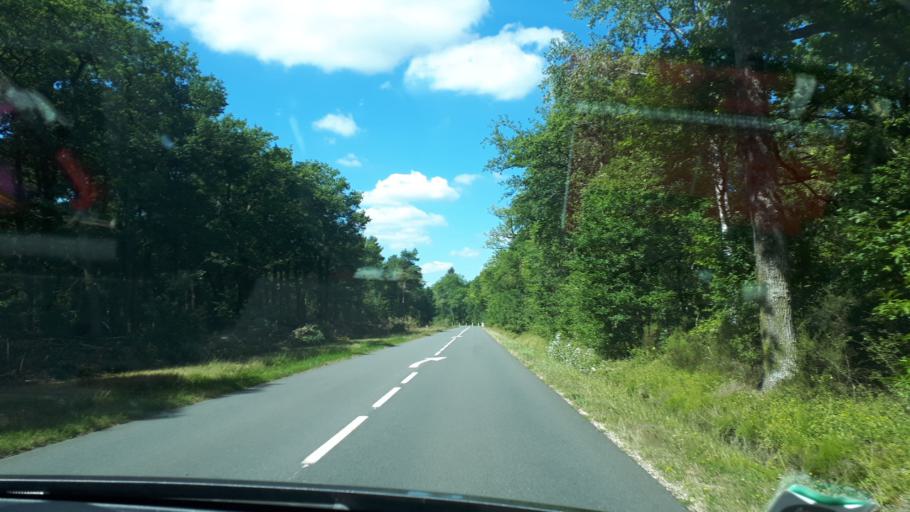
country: FR
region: Centre
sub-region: Departement du Loir-et-Cher
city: Neung-sur-Beuvron
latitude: 47.5337
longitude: 1.8190
